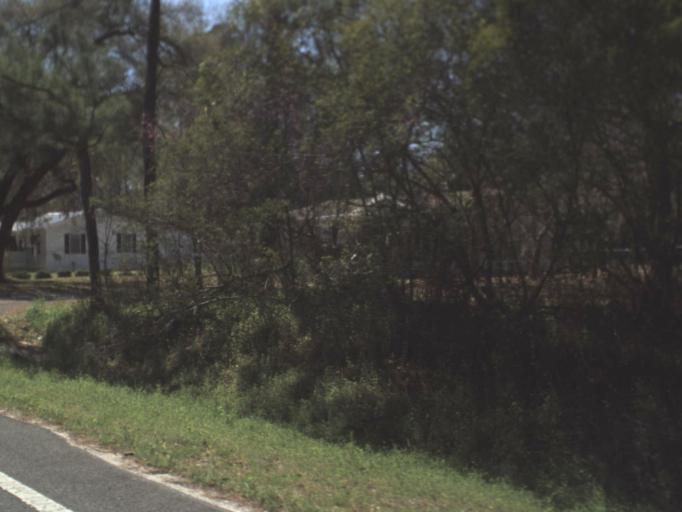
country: US
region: Florida
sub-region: Leon County
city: Woodville
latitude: 30.3077
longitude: -84.2462
